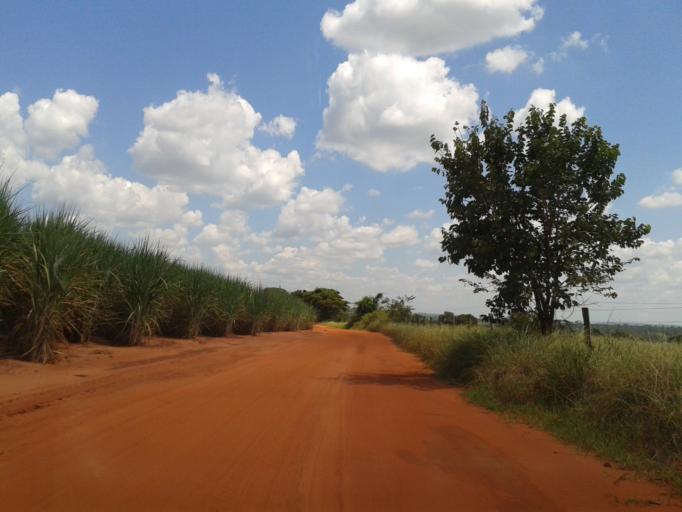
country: BR
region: Minas Gerais
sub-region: Ituiutaba
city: Ituiutaba
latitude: -19.0237
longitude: -49.6909
